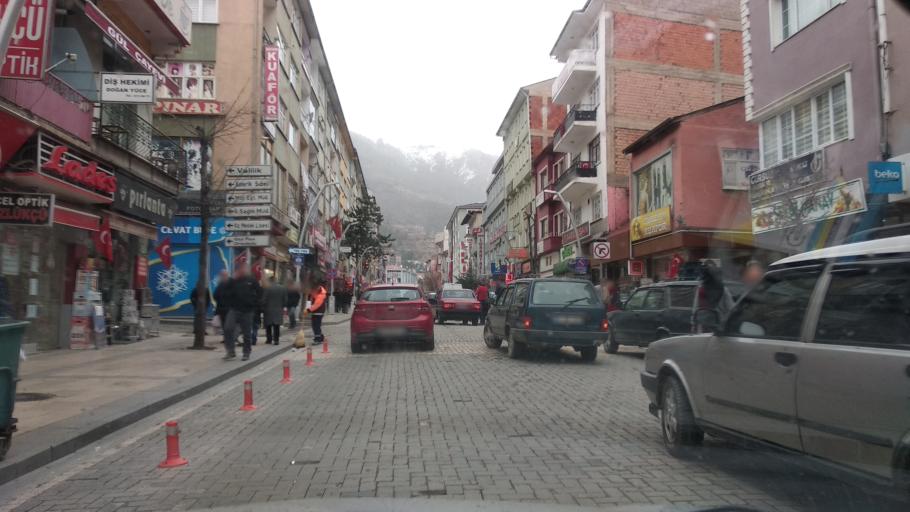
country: TR
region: Gumushane
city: Gumushkhane
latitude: 40.4589
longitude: 39.4793
